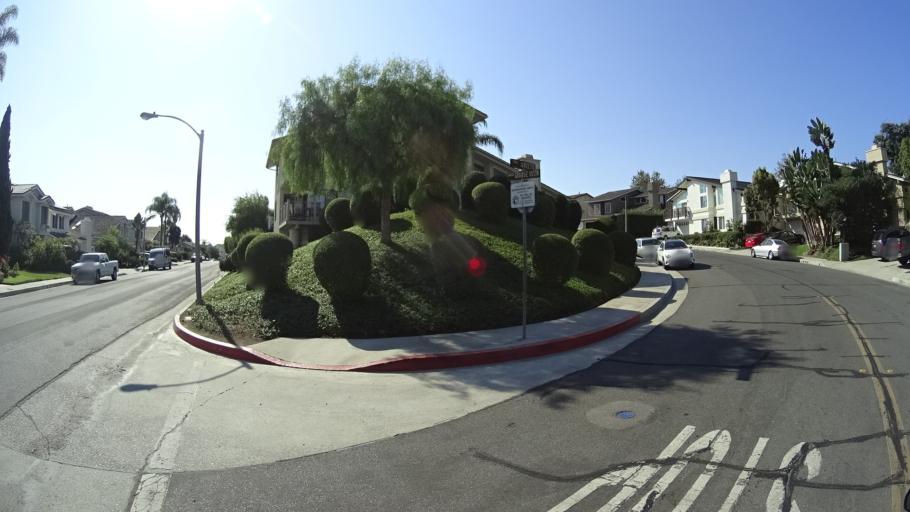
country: US
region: California
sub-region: Orange County
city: San Clemente
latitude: 33.4533
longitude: -117.6493
